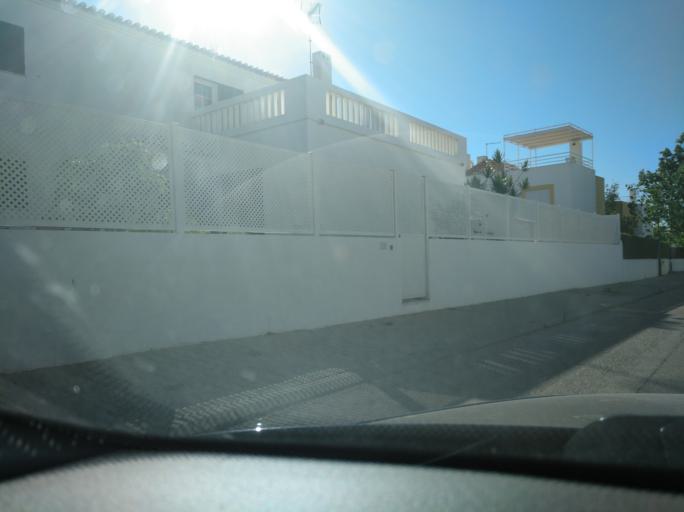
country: PT
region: Faro
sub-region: Vila Real de Santo Antonio
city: Monte Gordo
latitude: 37.1697
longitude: -7.5152
